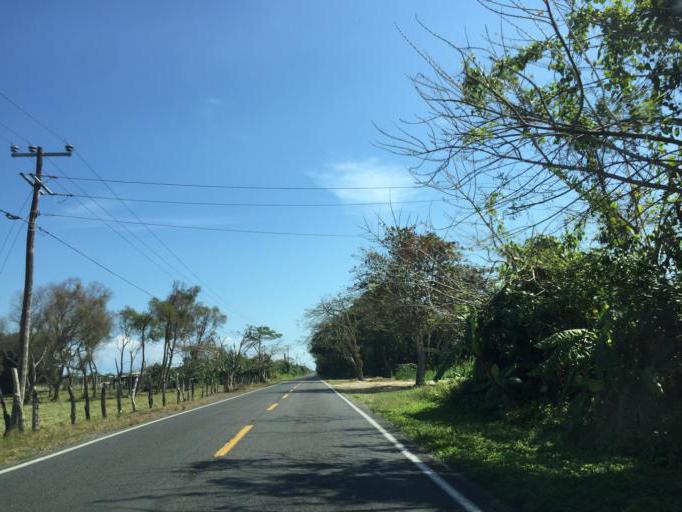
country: MX
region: Veracruz
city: Tecolutla
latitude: 20.4756
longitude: -97.0394
